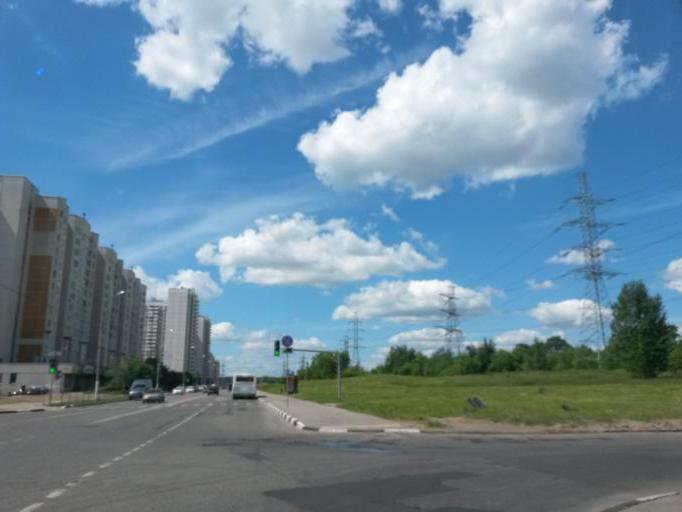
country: RU
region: Moscow
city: Annino
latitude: 55.5754
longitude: 37.5888
